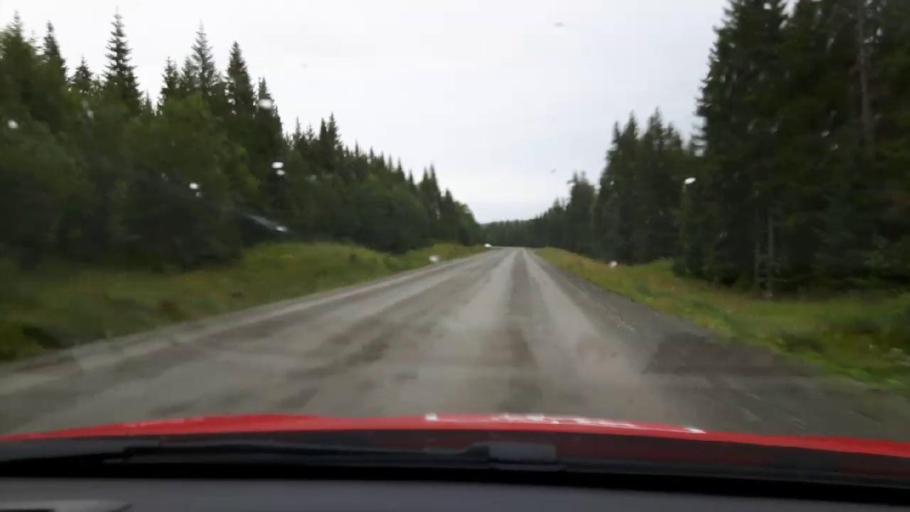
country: SE
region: Jaemtland
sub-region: Are Kommun
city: Are
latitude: 63.4525
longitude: 12.6510
